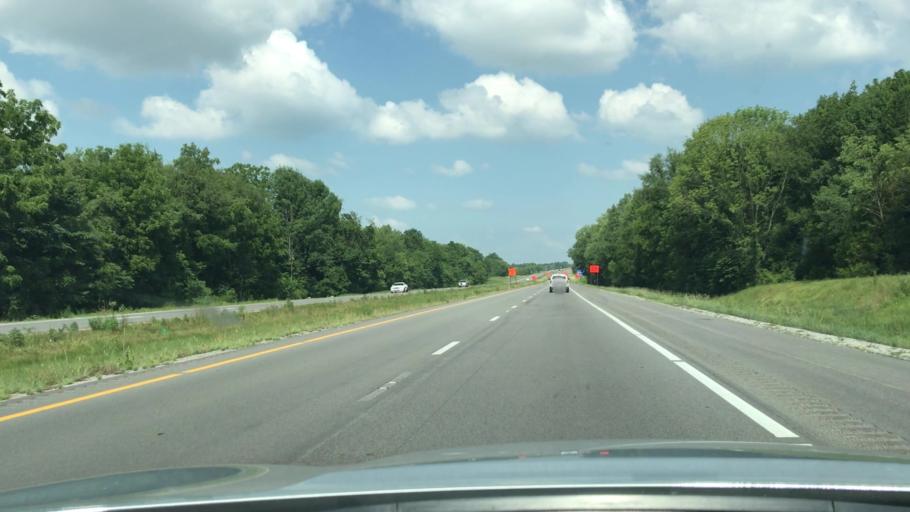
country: US
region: Kentucky
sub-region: Warren County
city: Bowling Green
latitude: 36.9360
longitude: -86.4662
